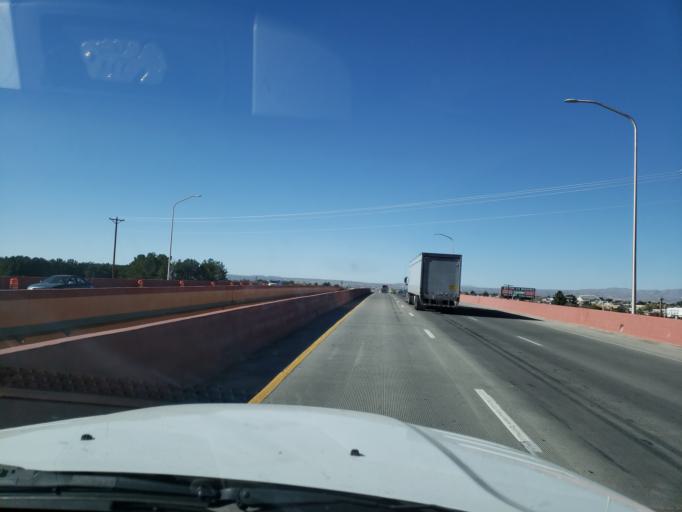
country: US
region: New Mexico
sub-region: Dona Ana County
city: University Park
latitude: 32.2811
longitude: -106.7697
